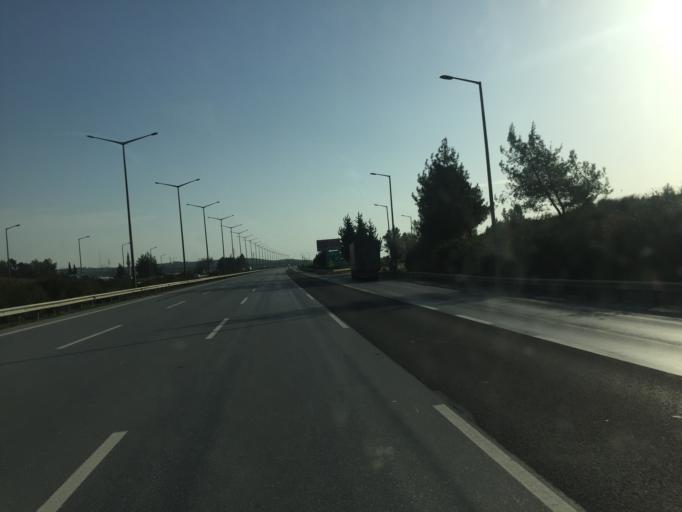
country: TR
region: Mersin
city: Yenice
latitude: 37.0235
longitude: 35.0593
